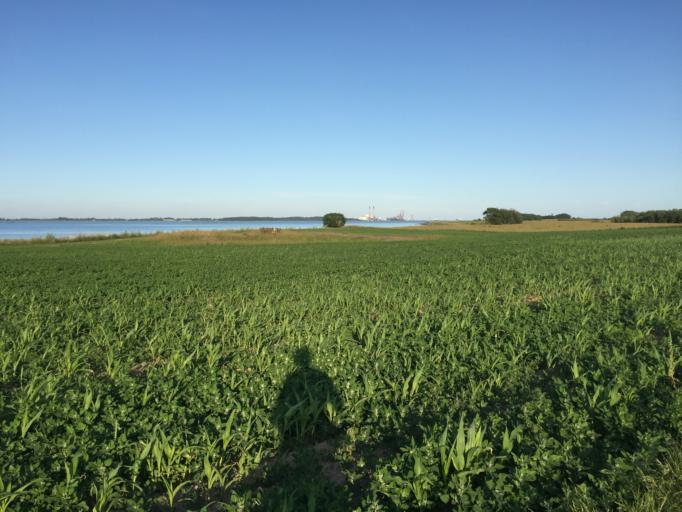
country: DK
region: Zealand
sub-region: Slagelse Kommune
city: Korsor
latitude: 55.2294
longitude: 11.1780
